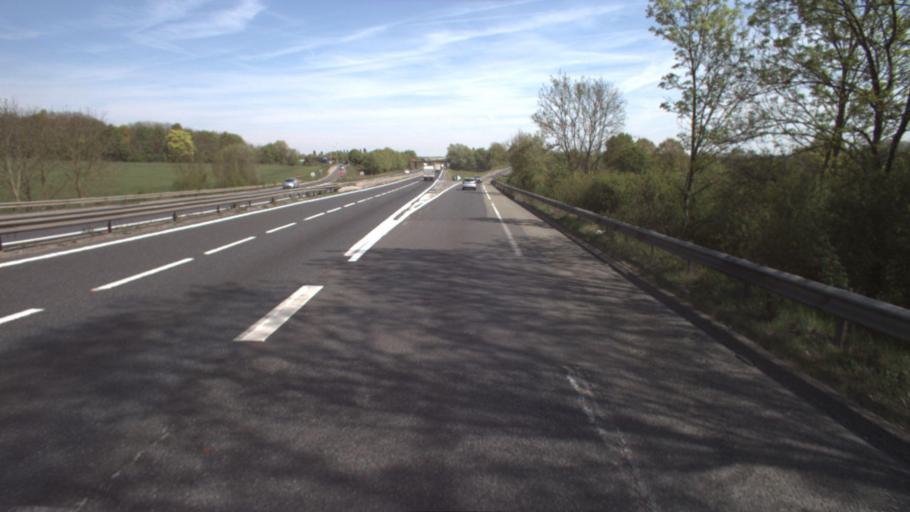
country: FR
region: Ile-de-France
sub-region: Departement de Seine-et-Marne
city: Saint-Mard
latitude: 49.0547
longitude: 2.6997
